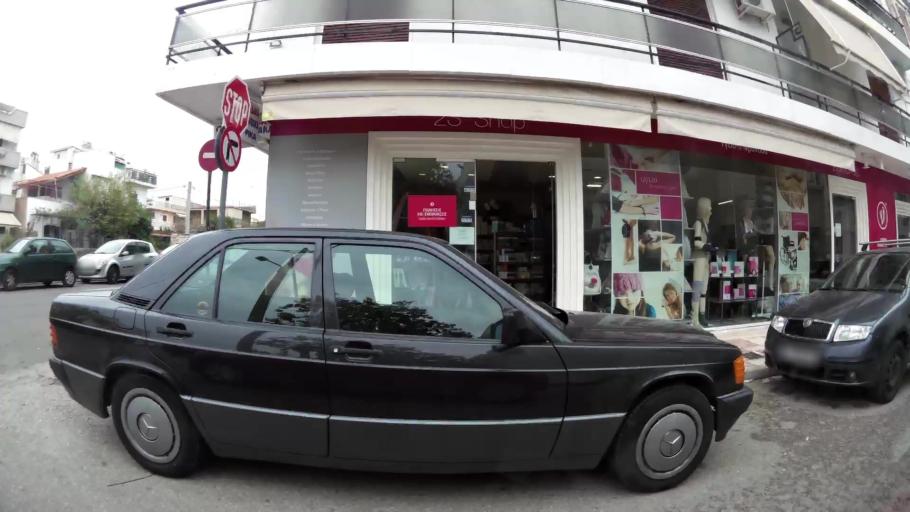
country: GR
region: Attica
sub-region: Nomarchia Athinas
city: Agioi Anargyroi
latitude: 38.0333
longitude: 23.7155
